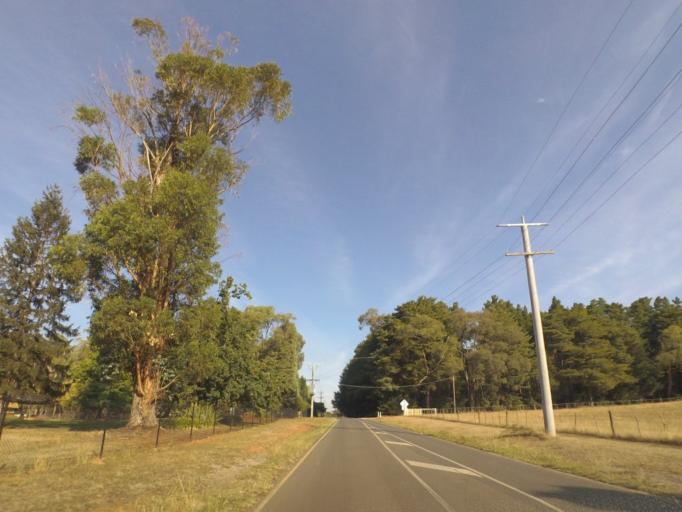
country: AU
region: Victoria
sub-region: Yarra Ranges
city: Macclesfield
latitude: -37.8145
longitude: 145.4568
